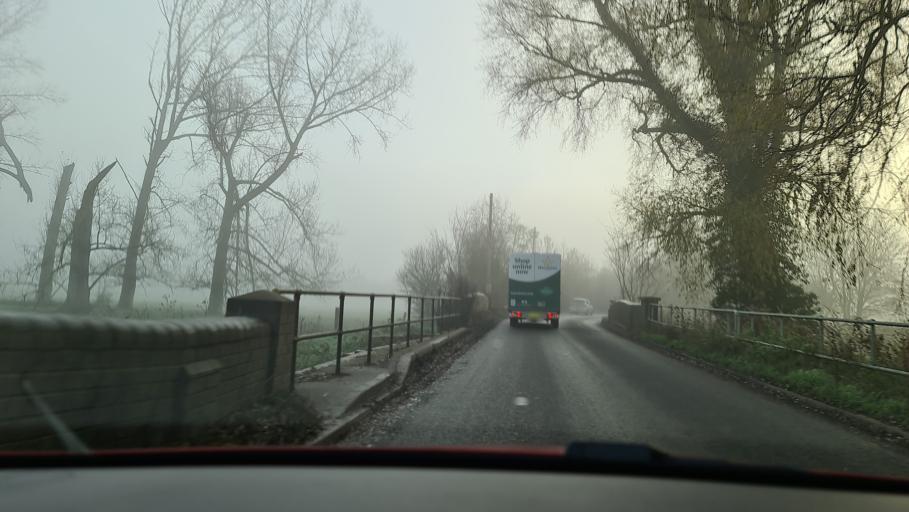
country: GB
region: England
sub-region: Buckinghamshire
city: Haddenham
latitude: 51.7959
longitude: -0.9452
